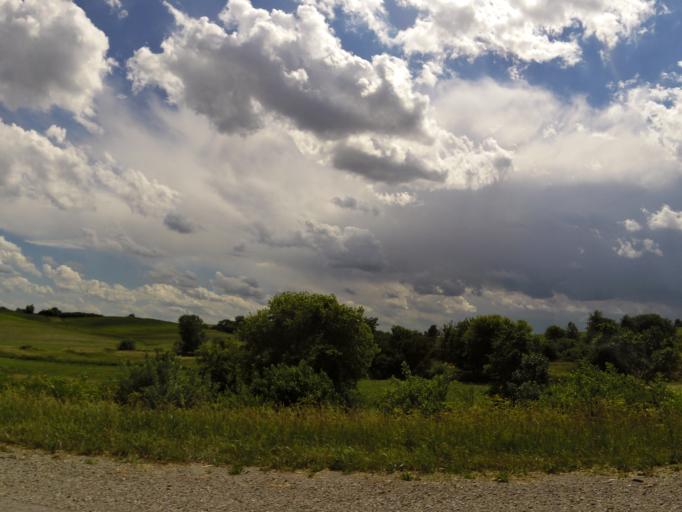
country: US
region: Iowa
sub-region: Johnson County
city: University Heights
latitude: 41.6438
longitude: -91.5797
